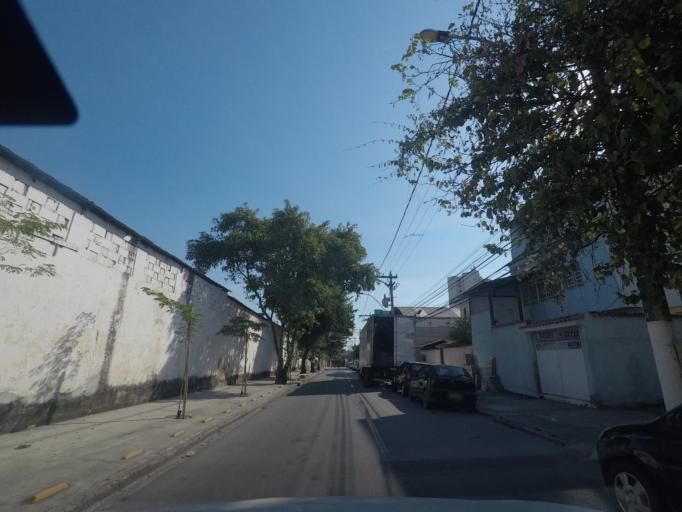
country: BR
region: Rio de Janeiro
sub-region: Niteroi
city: Niteroi
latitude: -22.8834
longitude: -43.1251
